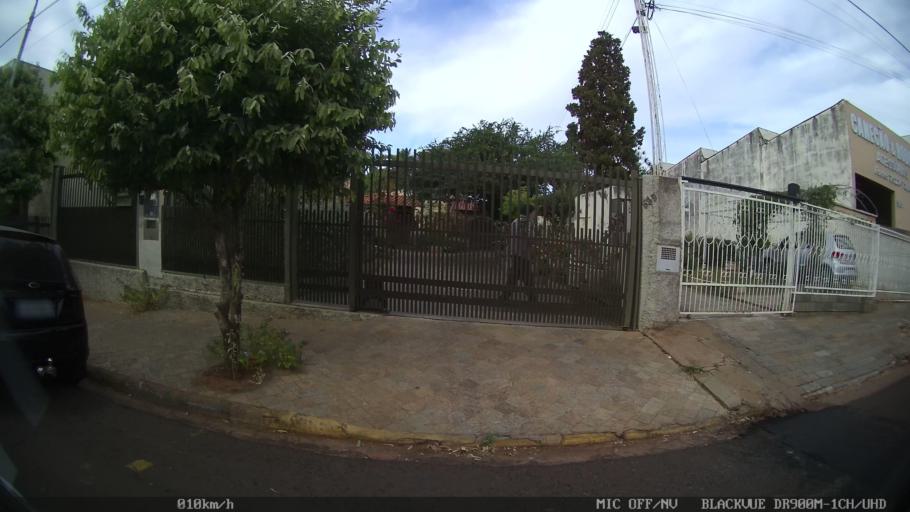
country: BR
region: Sao Paulo
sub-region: Catanduva
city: Catanduva
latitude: -21.1430
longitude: -48.9773
